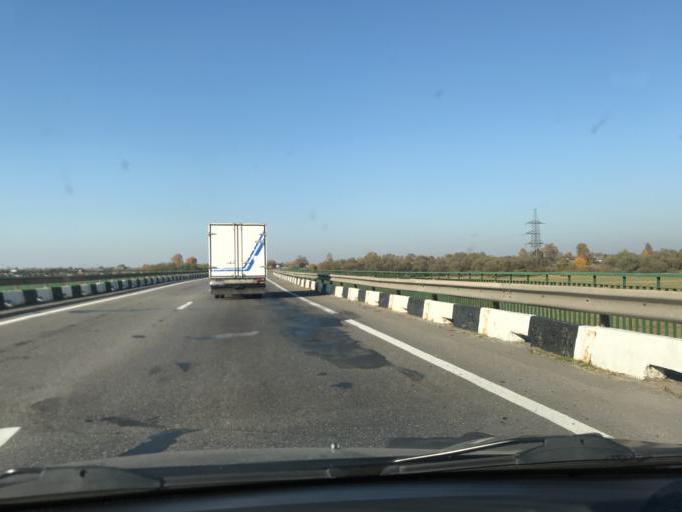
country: BY
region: Minsk
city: Dukora
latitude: 53.6640
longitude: 27.9409
